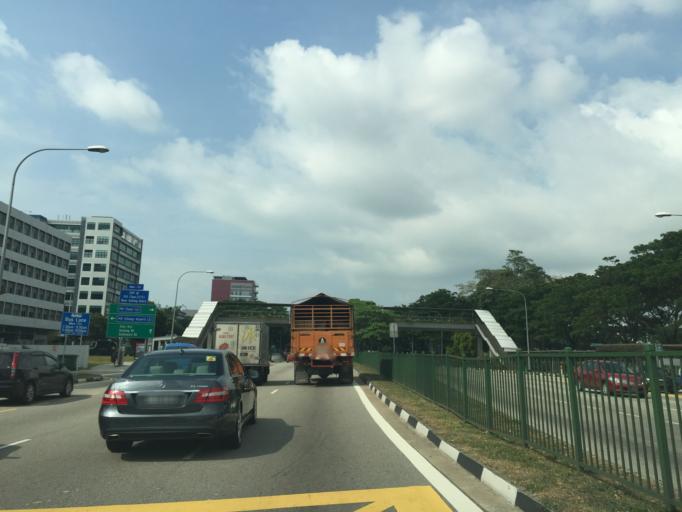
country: SG
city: Singapore
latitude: 1.3257
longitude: 103.8905
